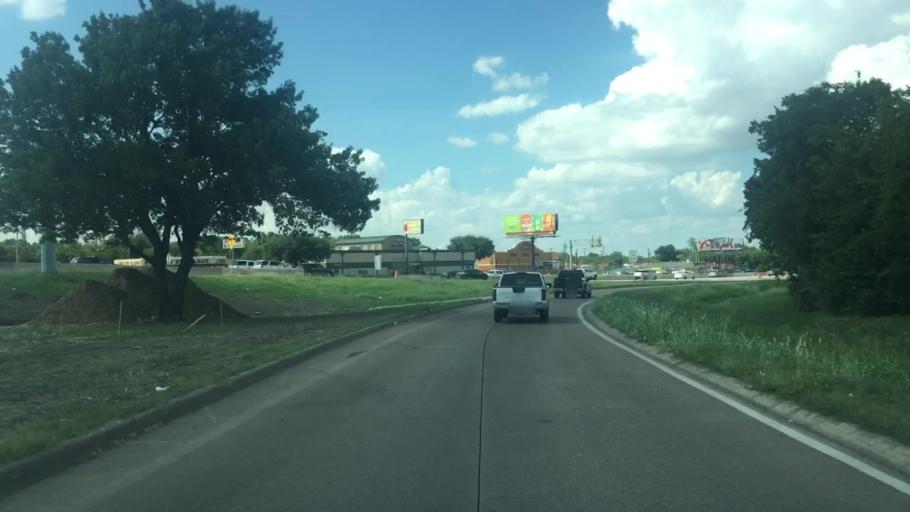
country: US
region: Texas
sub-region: Dallas County
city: Cockrell Hill
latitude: 32.7142
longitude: -96.8284
